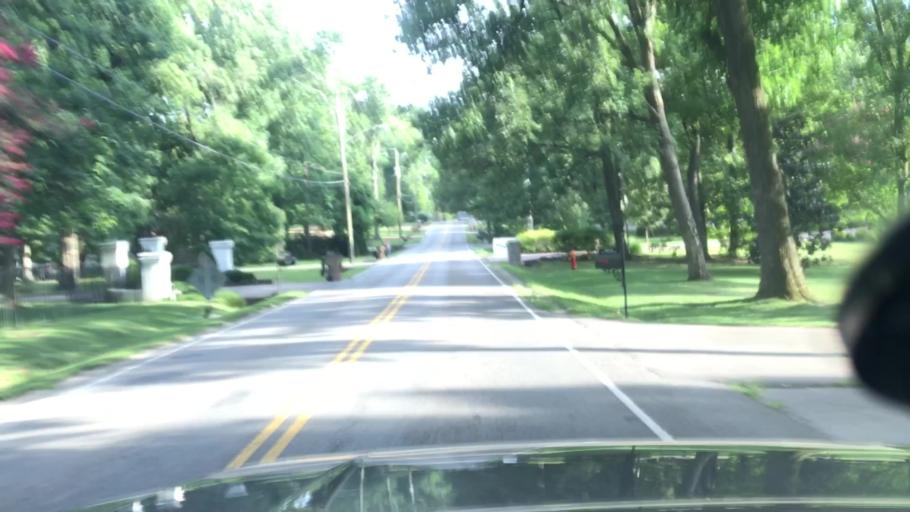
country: US
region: Tennessee
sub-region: Davidson County
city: Belle Meade
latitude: 36.0970
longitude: -86.8391
